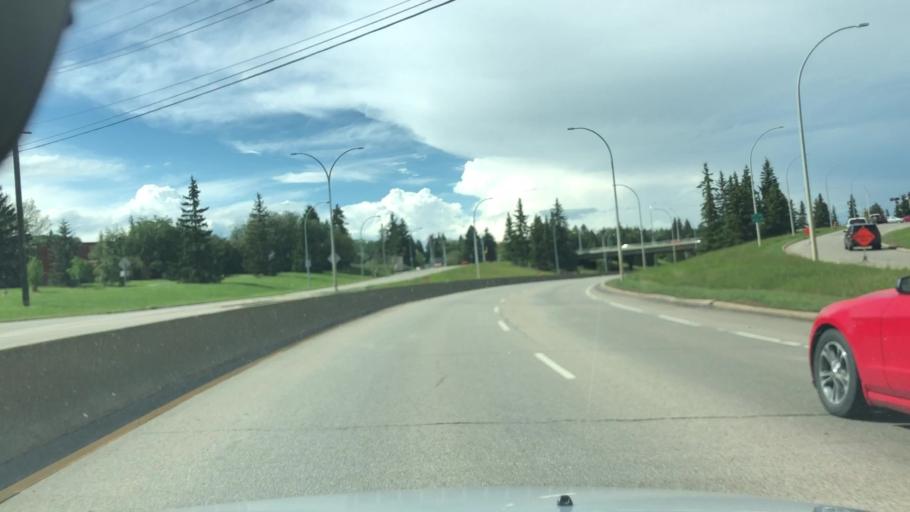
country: CA
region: Alberta
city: Edmonton
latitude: 53.5492
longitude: -113.5482
